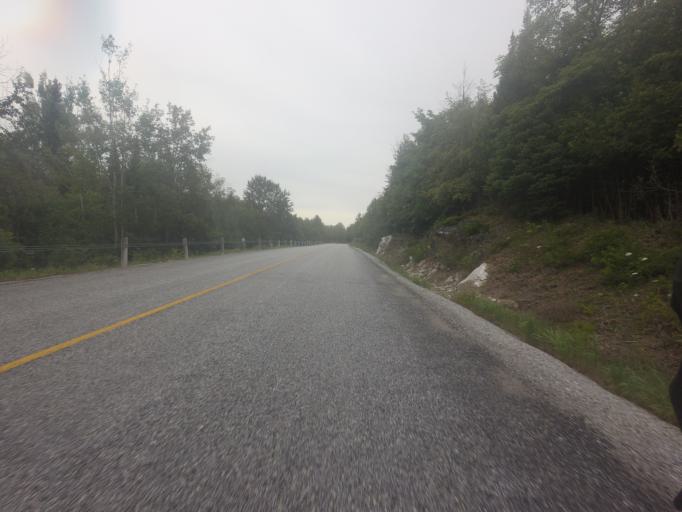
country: CA
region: Ontario
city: Perth
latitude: 44.9096
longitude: -76.4893
